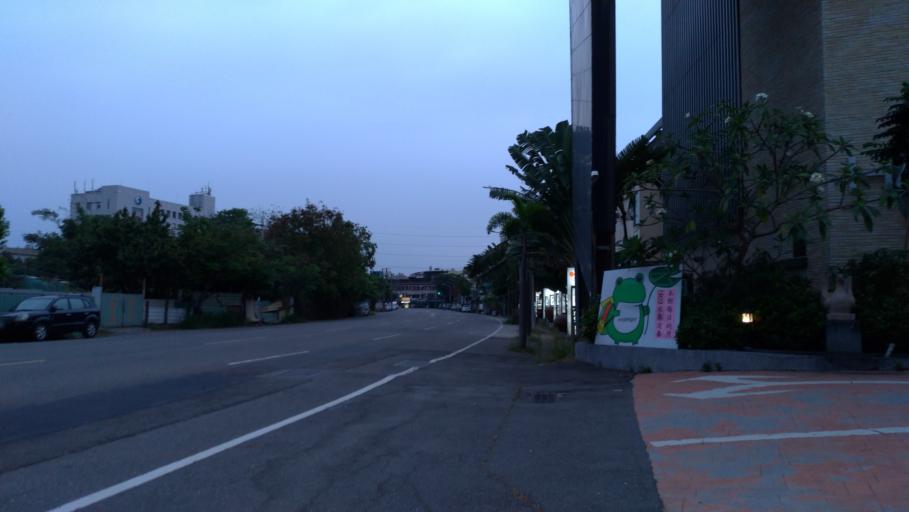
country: TW
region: Taiwan
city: Fengshan
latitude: 22.6558
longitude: 120.3616
